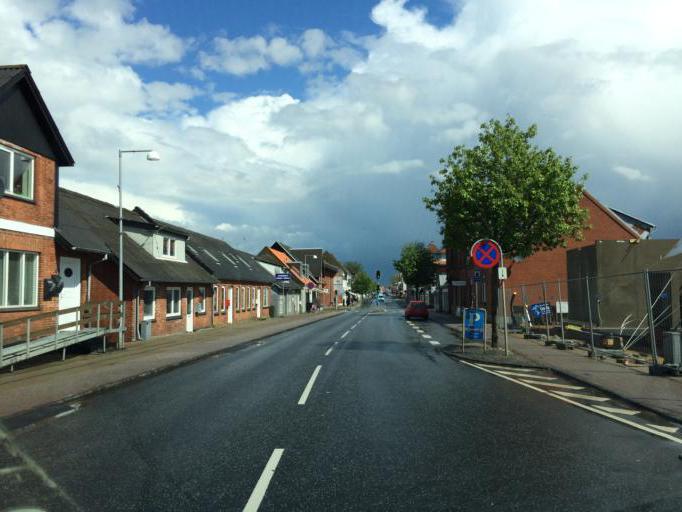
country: DK
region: Central Jutland
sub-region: Holstebro Kommune
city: Vinderup
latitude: 56.4792
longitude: 8.7778
